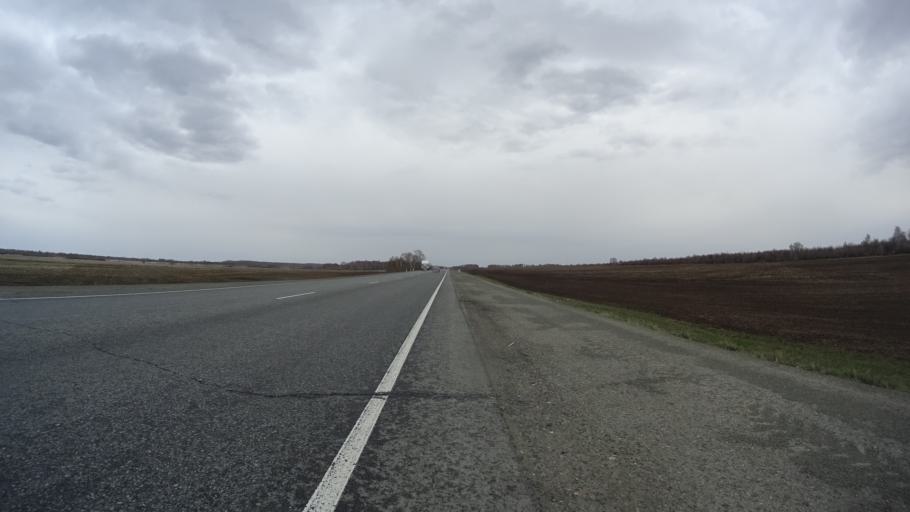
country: RU
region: Chelyabinsk
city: Krasnogorskiy
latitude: 54.6674
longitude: 61.2520
